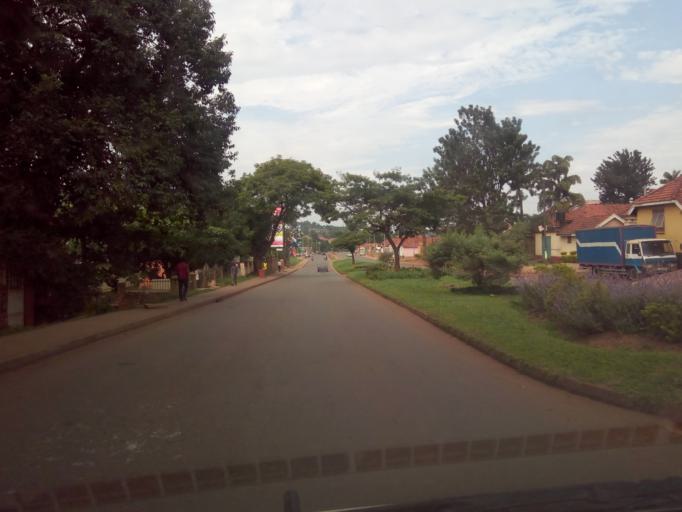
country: UG
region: Central Region
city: Kampala Central Division
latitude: 0.3434
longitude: 32.5921
